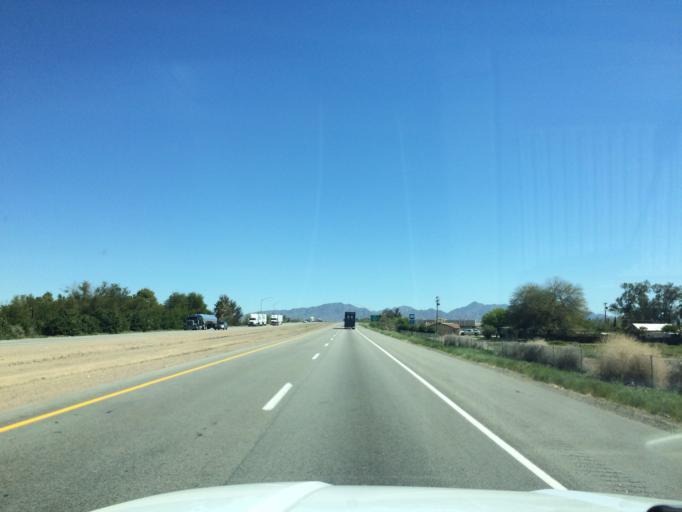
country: US
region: California
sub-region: Riverside County
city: Blythe
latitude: 33.6072
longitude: -114.5785
